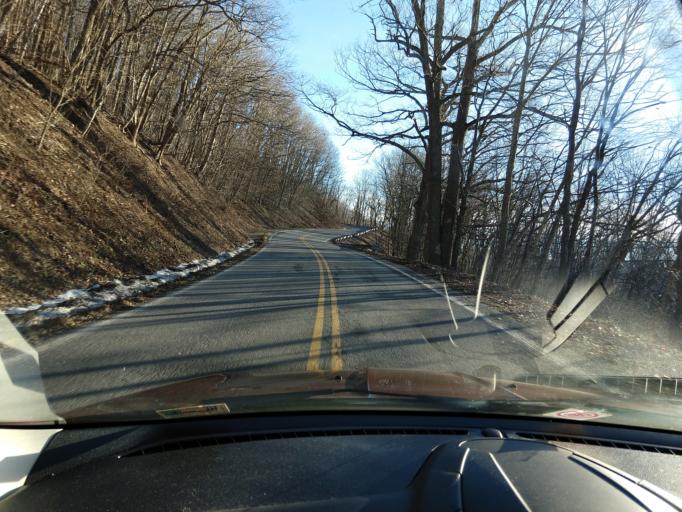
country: US
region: Virginia
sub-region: Alleghany County
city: Clifton Forge
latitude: 37.8792
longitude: -79.8887
